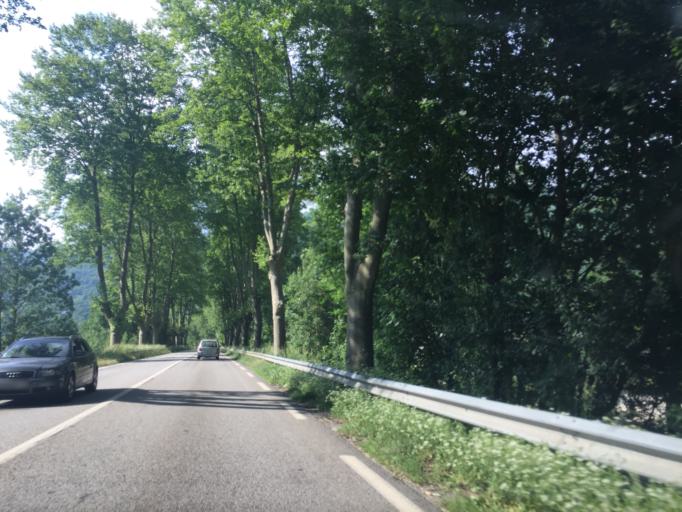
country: FR
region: Rhone-Alpes
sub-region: Departement de la Savoie
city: Aiton
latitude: 45.5483
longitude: 6.2960
